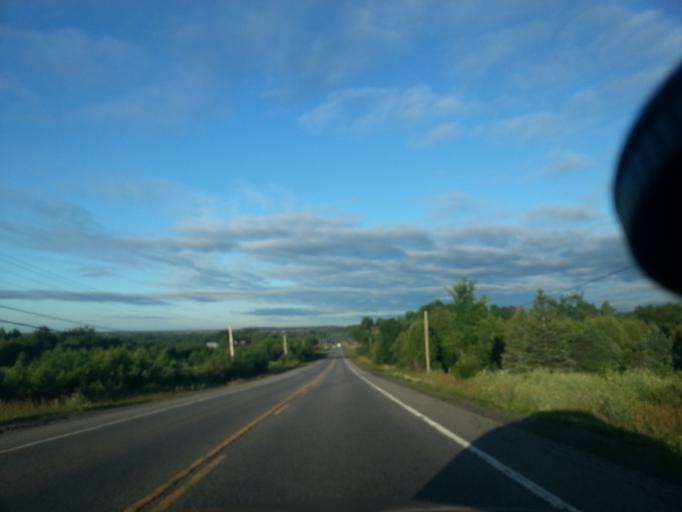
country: CA
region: Ontario
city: Carleton Place
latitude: 45.2815
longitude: -76.1078
